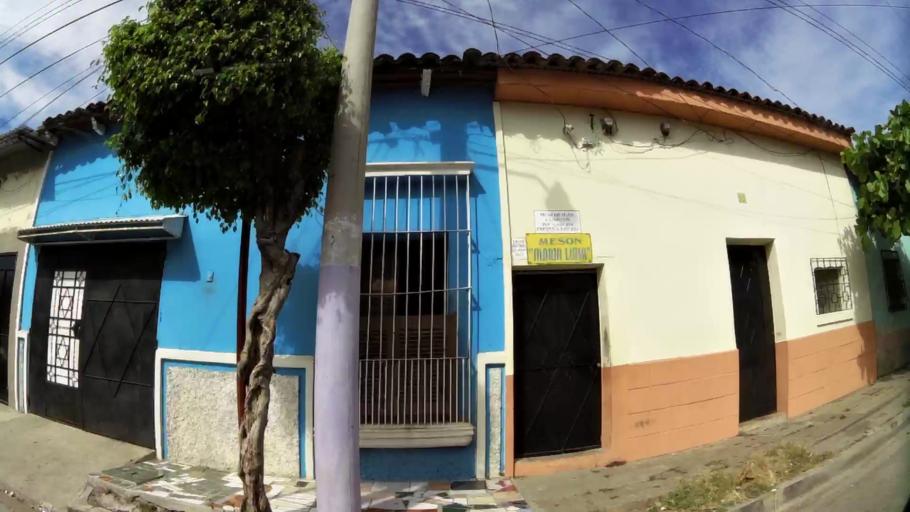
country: SV
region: Santa Ana
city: Chalchuapa
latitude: 13.9826
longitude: -89.6764
